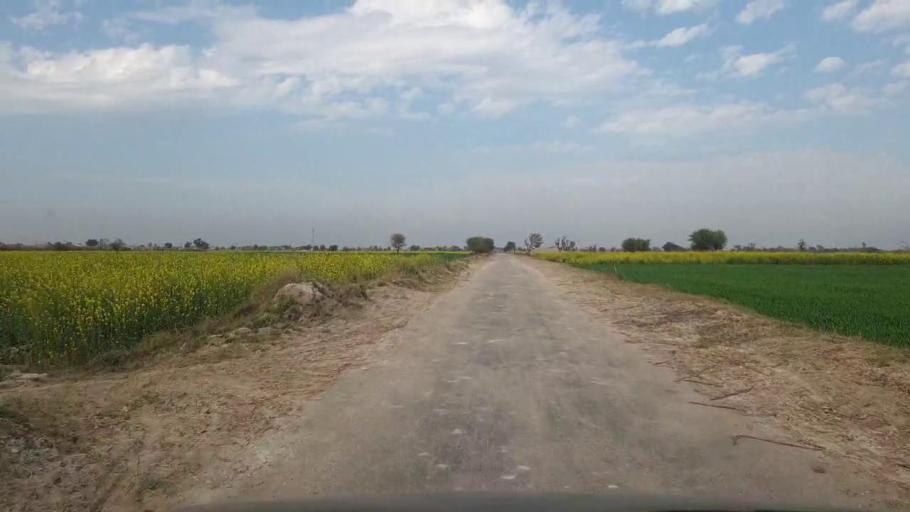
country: PK
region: Sindh
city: Hala
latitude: 26.0012
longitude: 68.4145
